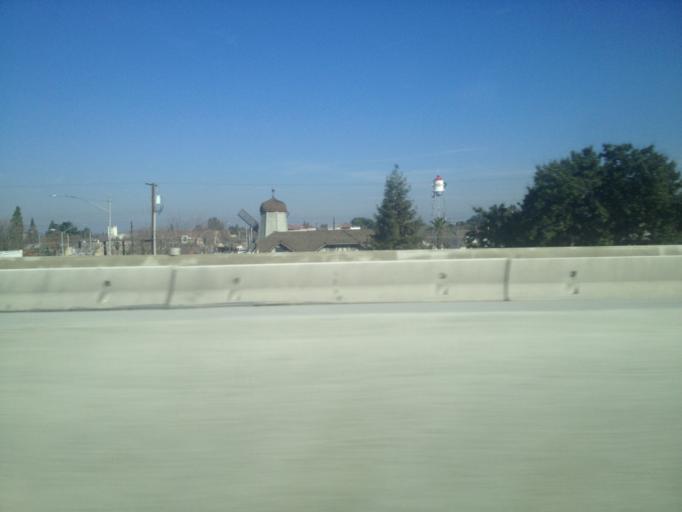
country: US
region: California
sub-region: Fresno County
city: Kingsburg
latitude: 36.5127
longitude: -119.5552
